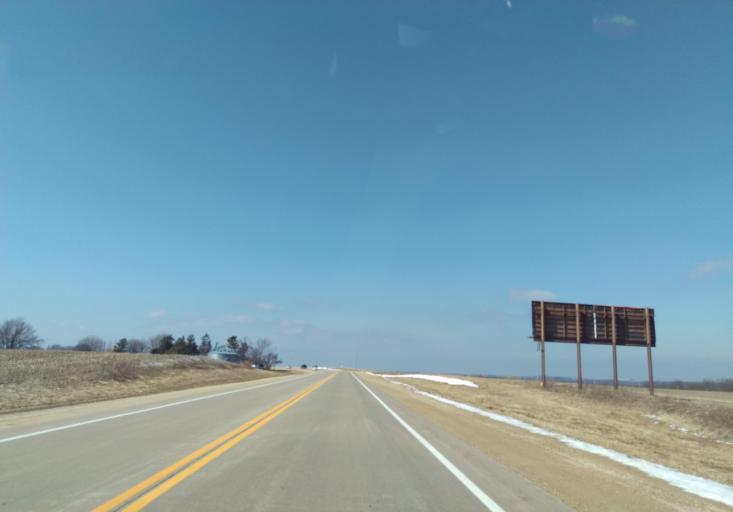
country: US
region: Wisconsin
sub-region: La Crosse County
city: La Crosse
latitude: 43.7303
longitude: -91.0914
